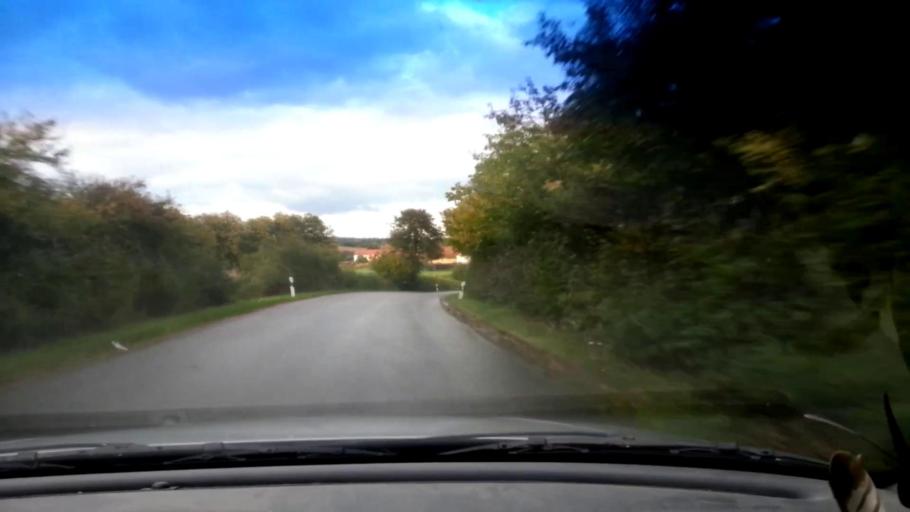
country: DE
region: Bavaria
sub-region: Upper Franconia
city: Burgebrach
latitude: 49.8163
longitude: 10.6721
